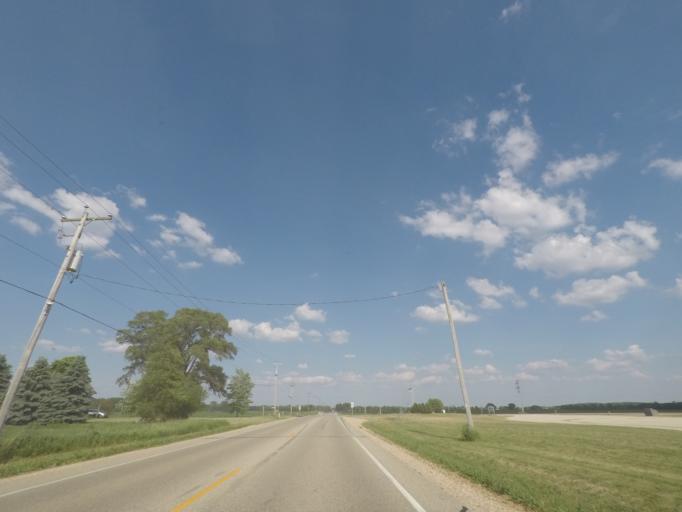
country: US
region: Wisconsin
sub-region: Walworth County
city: East Troy
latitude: 42.7927
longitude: -88.4462
